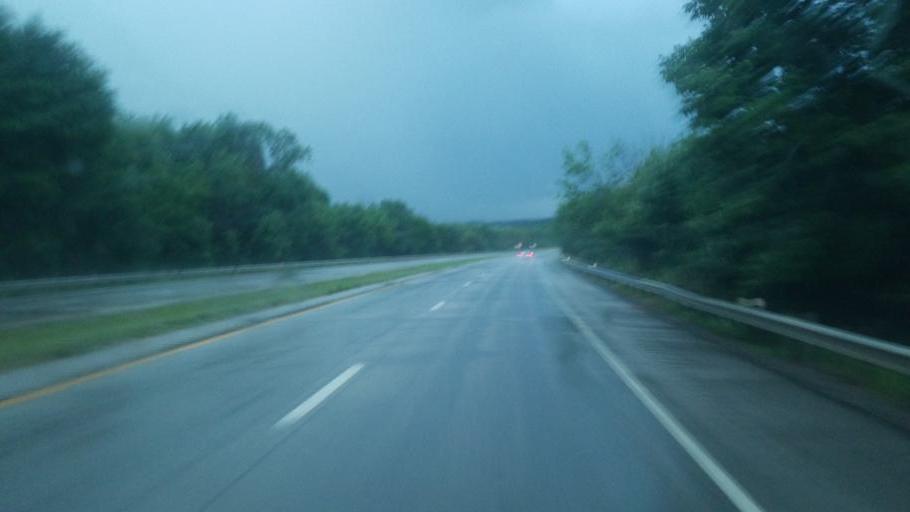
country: US
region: Ohio
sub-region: Summit County
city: Clinton
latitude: 40.9302
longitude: -81.6507
